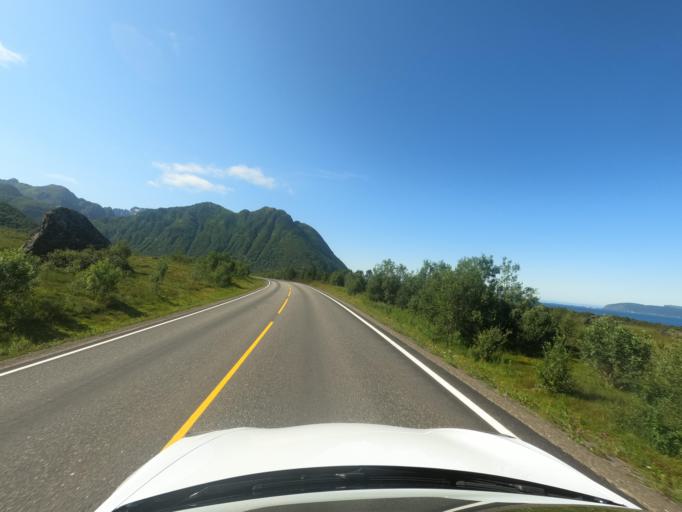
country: NO
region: Nordland
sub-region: Hadsel
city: Stokmarknes
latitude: 68.4581
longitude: 15.0657
